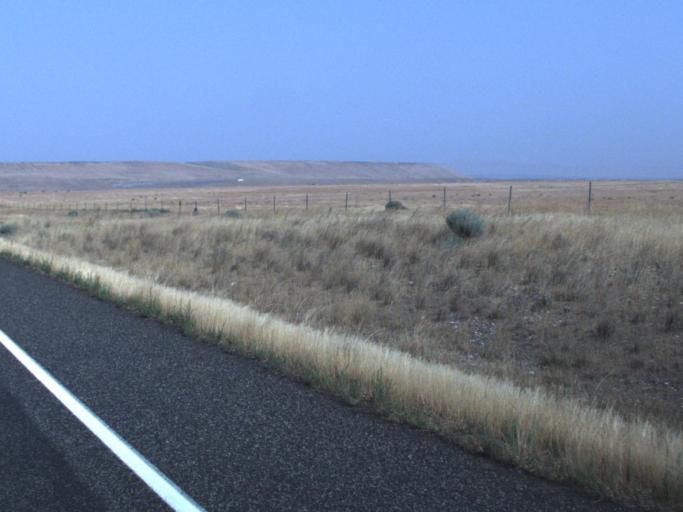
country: US
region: Washington
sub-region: Grant County
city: Desert Aire
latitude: 46.6265
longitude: -119.7266
